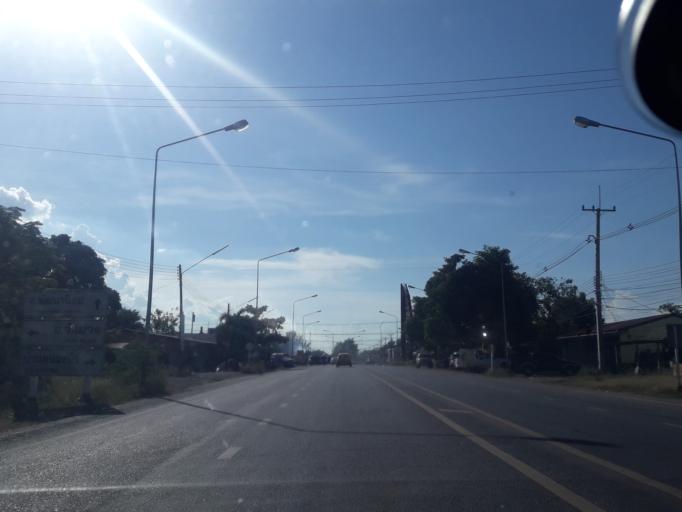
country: TH
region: Sara Buri
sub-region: Amphoe Wang Muang
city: Wang Muang
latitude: 14.8628
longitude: 101.0584
